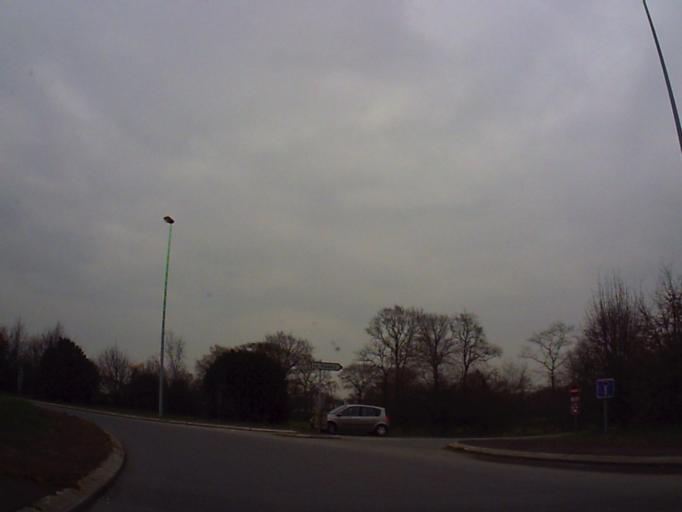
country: FR
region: Brittany
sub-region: Departement d'Ille-et-Vilaine
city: Saint-Gregoire
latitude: 48.1443
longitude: -1.6566
